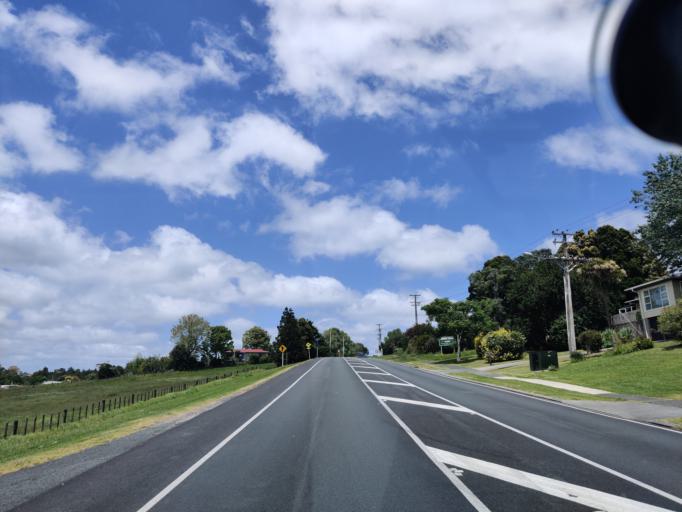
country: NZ
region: Auckland
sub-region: Auckland
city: Wellsford
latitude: -36.2843
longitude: 174.5201
